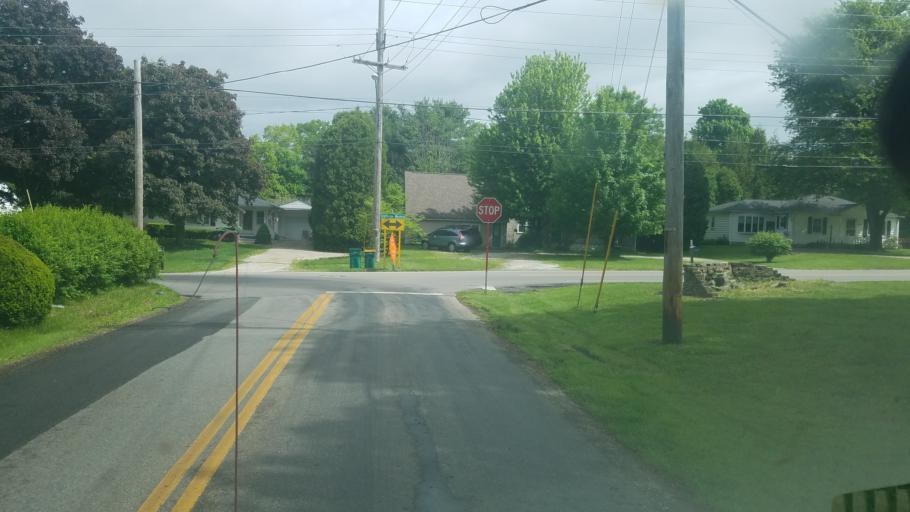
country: US
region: Ohio
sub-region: Wayne County
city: Smithville
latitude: 40.8575
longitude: -81.9159
